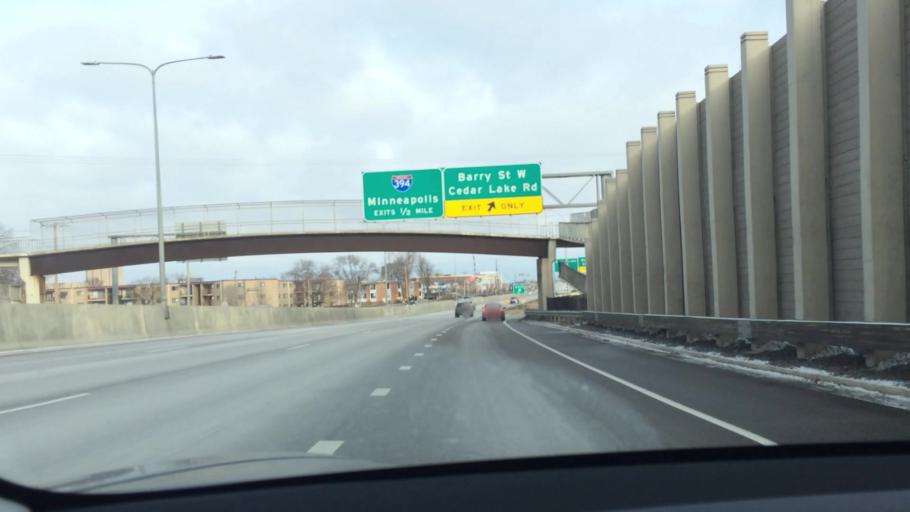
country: US
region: Minnesota
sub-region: Hennepin County
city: Saint Louis Park
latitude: 44.9551
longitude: -93.3475
